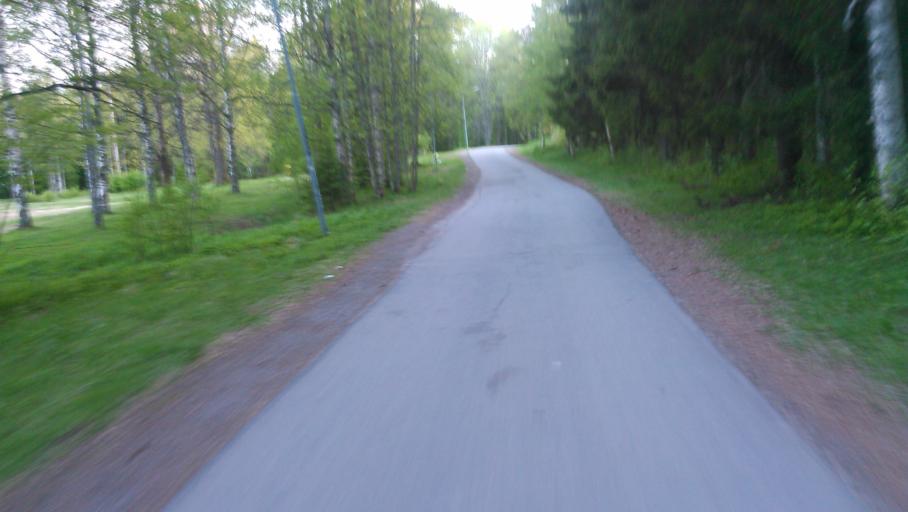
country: SE
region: Vaesterbotten
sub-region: Umea Kommun
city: Ersmark
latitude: 63.8334
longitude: 20.3144
